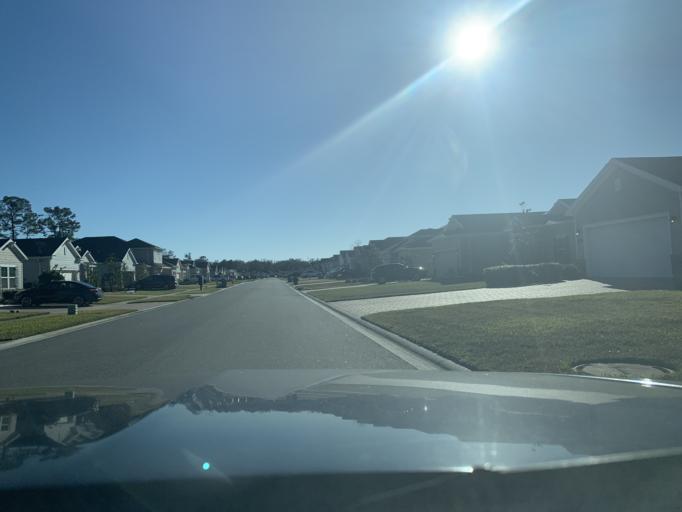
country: US
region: Florida
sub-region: Clay County
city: Green Cove Springs
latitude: 29.9807
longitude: -81.5216
